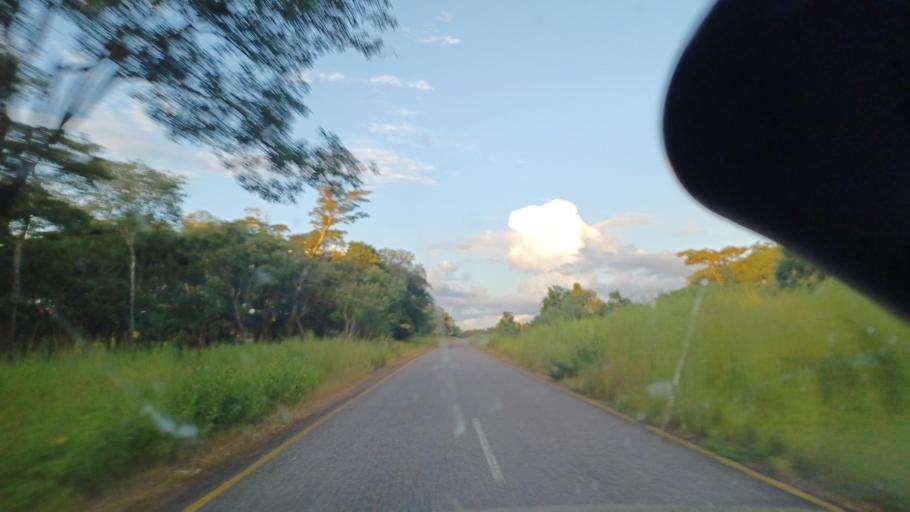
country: ZM
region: North-Western
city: Kasempa
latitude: -12.9865
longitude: 25.5284
